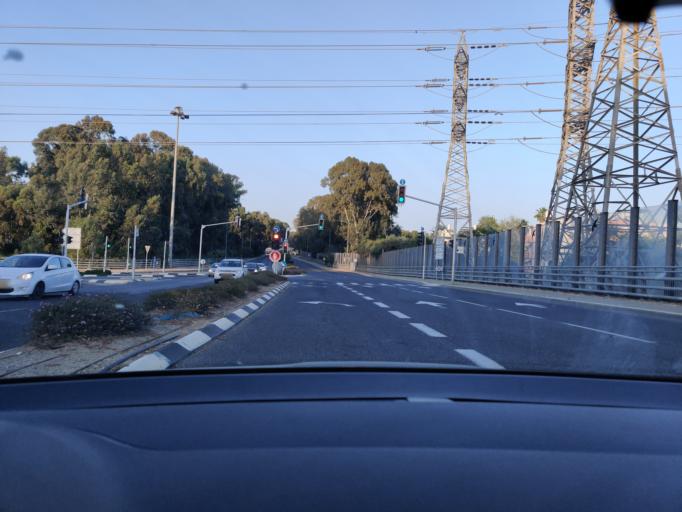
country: IL
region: Haifa
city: Hadera
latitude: 32.4790
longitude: 34.9554
